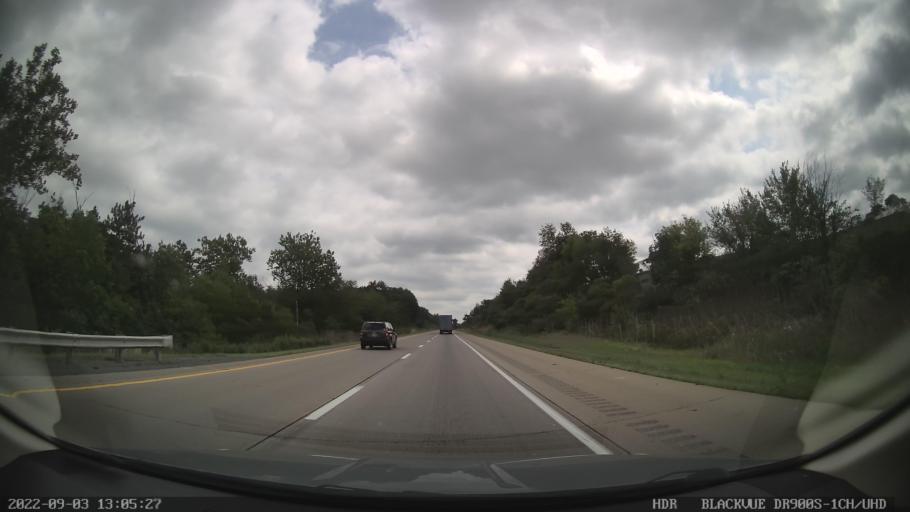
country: US
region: Pennsylvania
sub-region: Northumberland County
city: Milton
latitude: 41.0040
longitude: -76.7587
